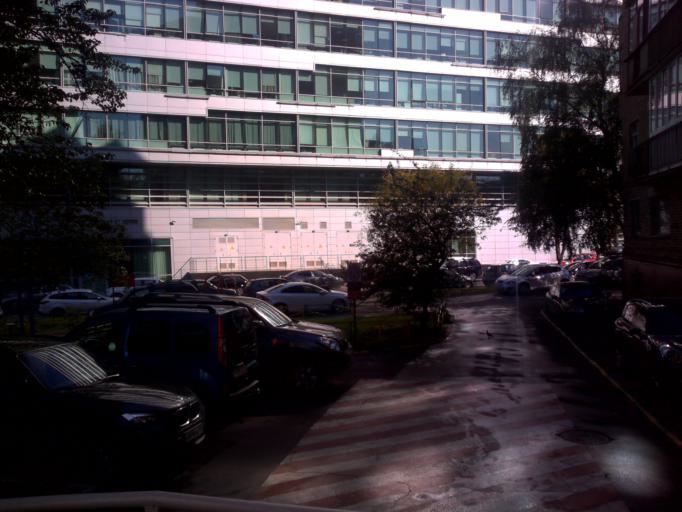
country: RU
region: Moskovskaya
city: Leninskiye Gory
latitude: 55.6922
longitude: 37.5750
